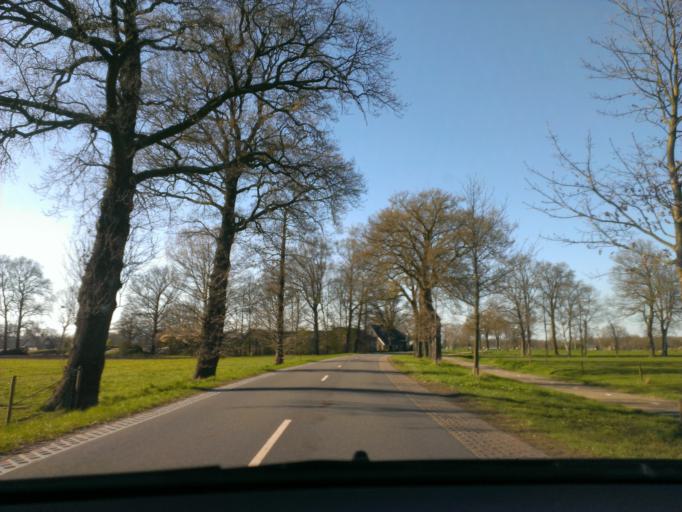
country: NL
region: Overijssel
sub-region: Gemeente Twenterand
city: Den Ham
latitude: 52.4368
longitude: 6.4745
